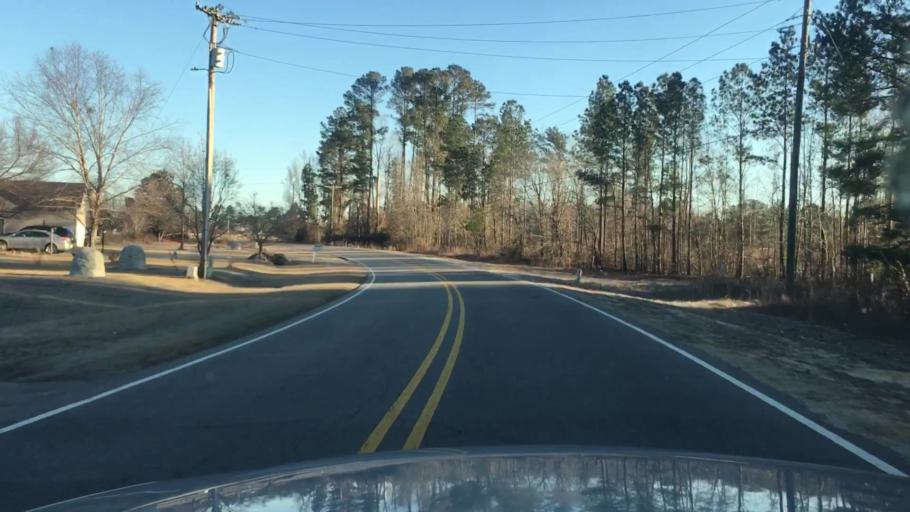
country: US
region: North Carolina
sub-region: Cumberland County
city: Hope Mills
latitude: 34.9643
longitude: -79.0083
